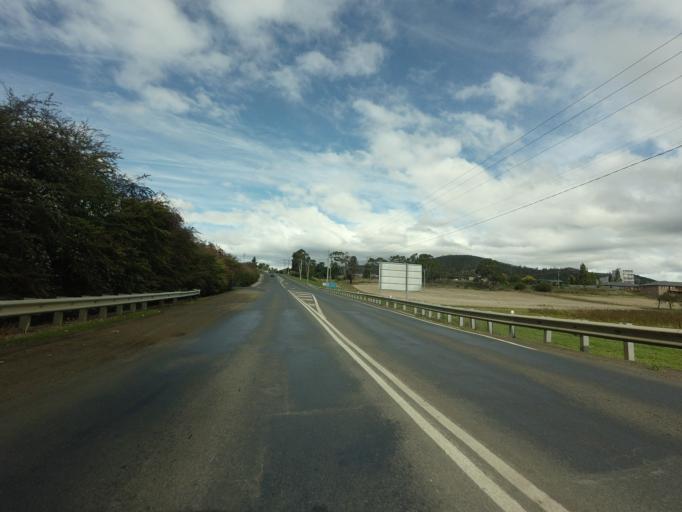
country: AU
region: Tasmania
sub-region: Derwent Valley
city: New Norfolk
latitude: -42.7788
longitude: 147.0715
